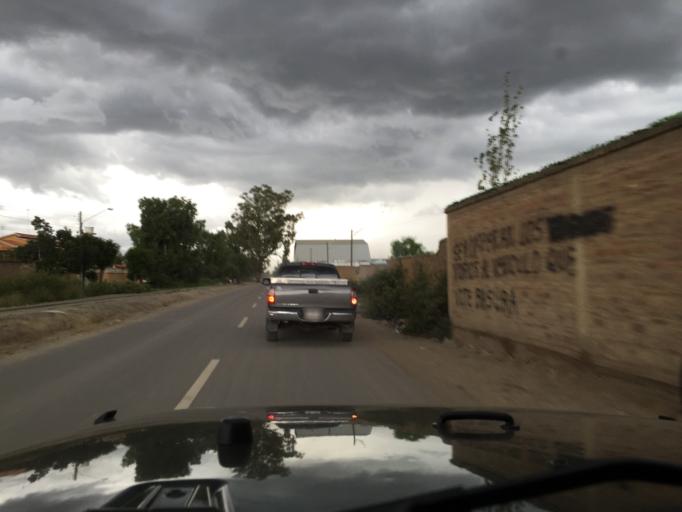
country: BO
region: Cochabamba
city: Cochabamba
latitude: -17.4000
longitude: -66.2023
